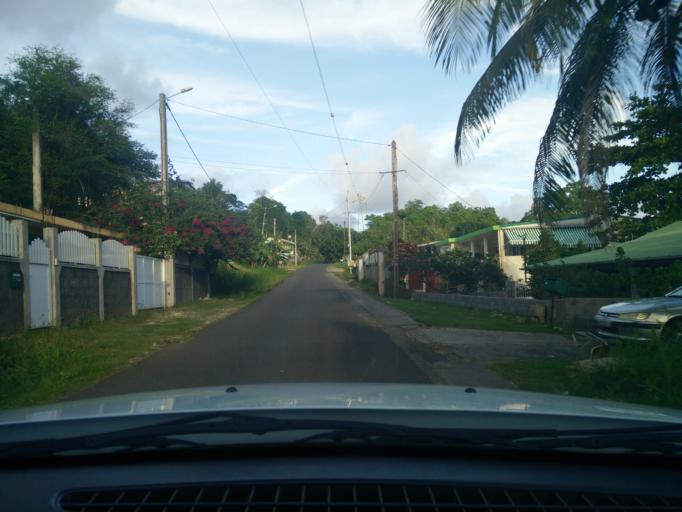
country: GP
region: Guadeloupe
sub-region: Guadeloupe
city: Les Abymes
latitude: 16.2503
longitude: -61.4982
